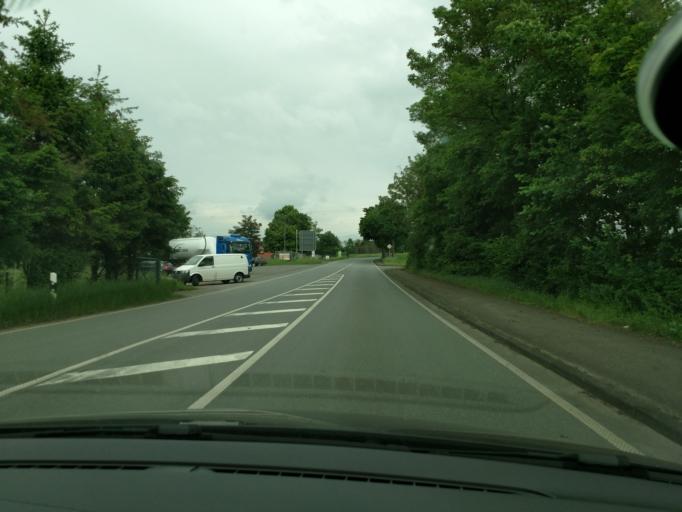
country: DE
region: Hesse
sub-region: Regierungsbezirk Kassel
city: Bad Arolsen
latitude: 51.3569
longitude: 8.9949
